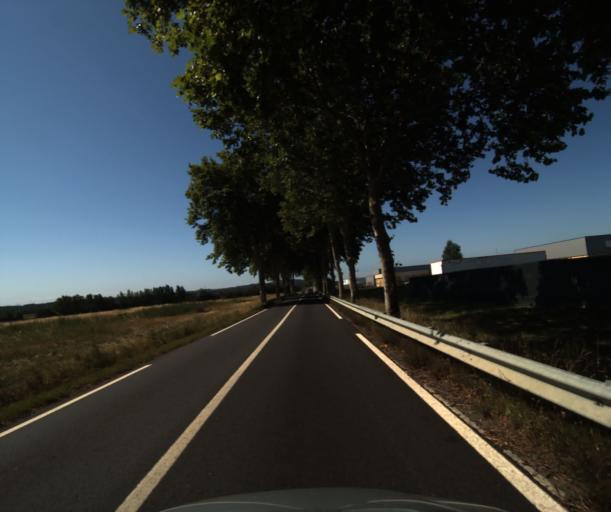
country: FR
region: Midi-Pyrenees
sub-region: Departement de la Haute-Garonne
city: Lagardelle-sur-Leze
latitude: 43.4186
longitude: 1.3742
